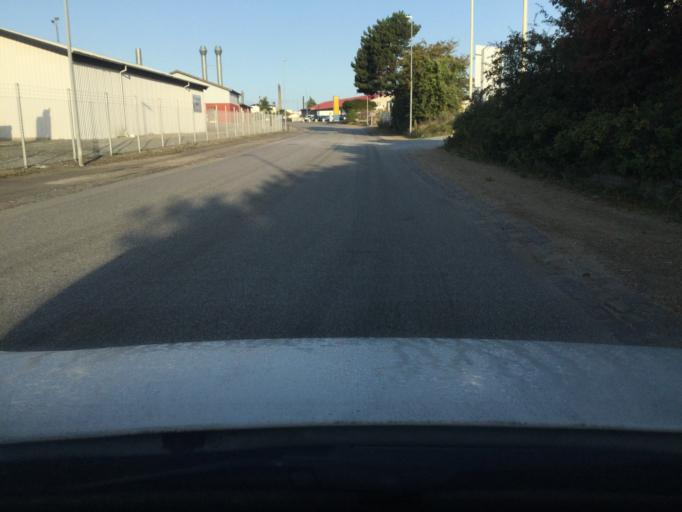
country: DK
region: Zealand
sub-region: Lolland Kommune
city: Nakskov
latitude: 54.8299
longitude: 11.1669
